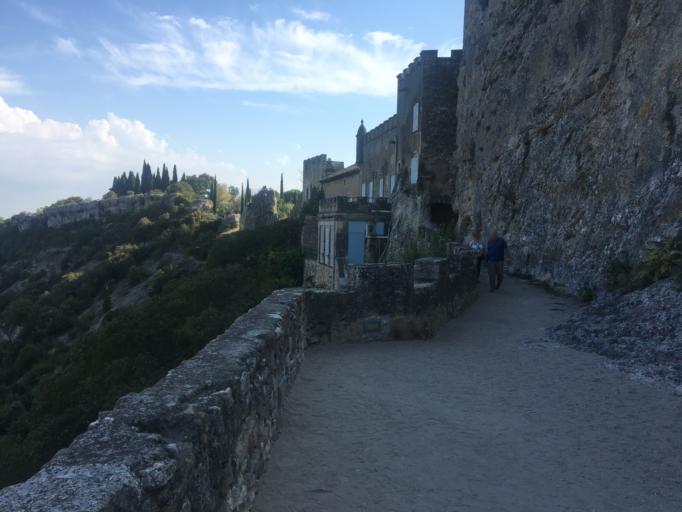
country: FR
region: Languedoc-Roussillon
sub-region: Departement du Gard
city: Saint-Julien-de-Peyrolas
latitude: 44.3034
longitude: 4.5567
